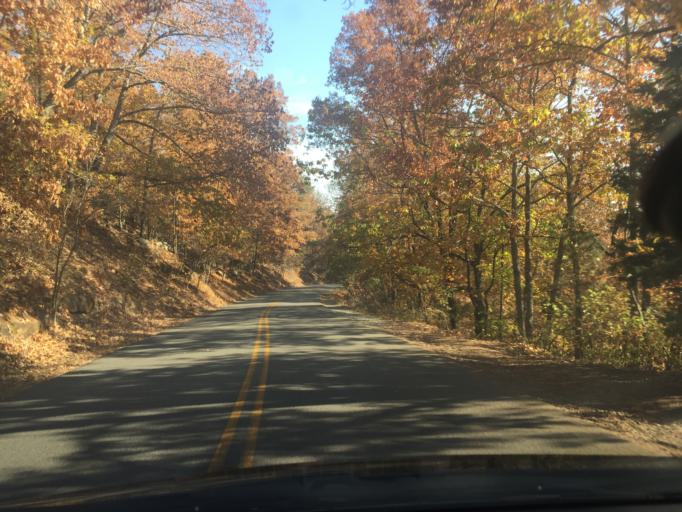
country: US
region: Georgia
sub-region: Cobb County
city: Marietta
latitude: 33.9788
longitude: -84.5738
